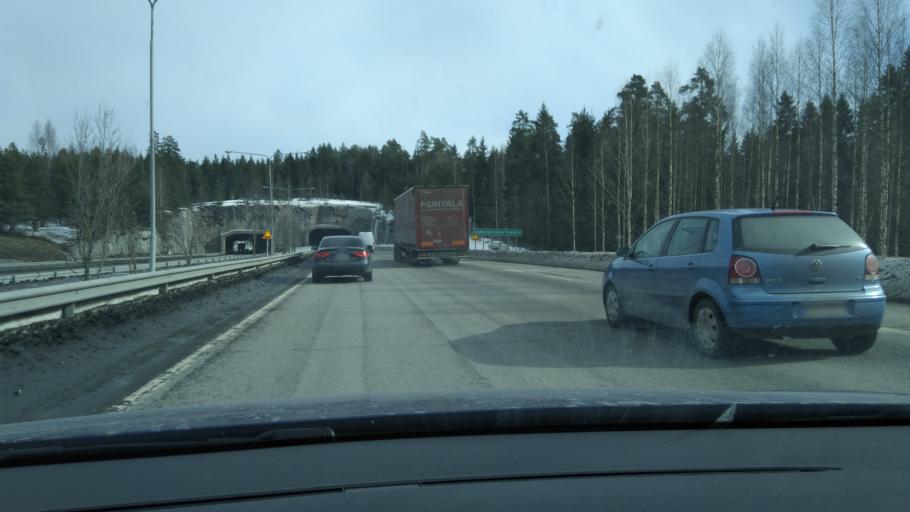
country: FI
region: Pirkanmaa
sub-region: Tampere
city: Tampere
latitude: 61.4619
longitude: 23.8022
